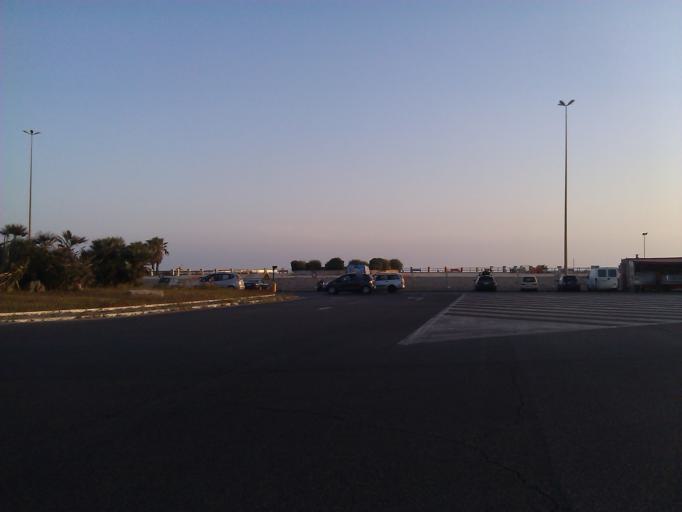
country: IT
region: Latium
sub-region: Citta metropolitana di Roma Capitale
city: Lido di Ostia
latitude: 41.7151
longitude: 12.3176
